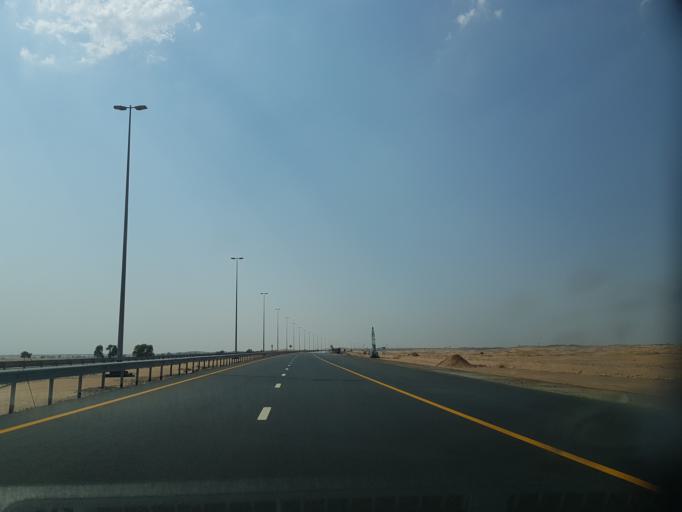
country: AE
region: Ash Shariqah
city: Adh Dhayd
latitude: 25.2595
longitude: 55.6825
